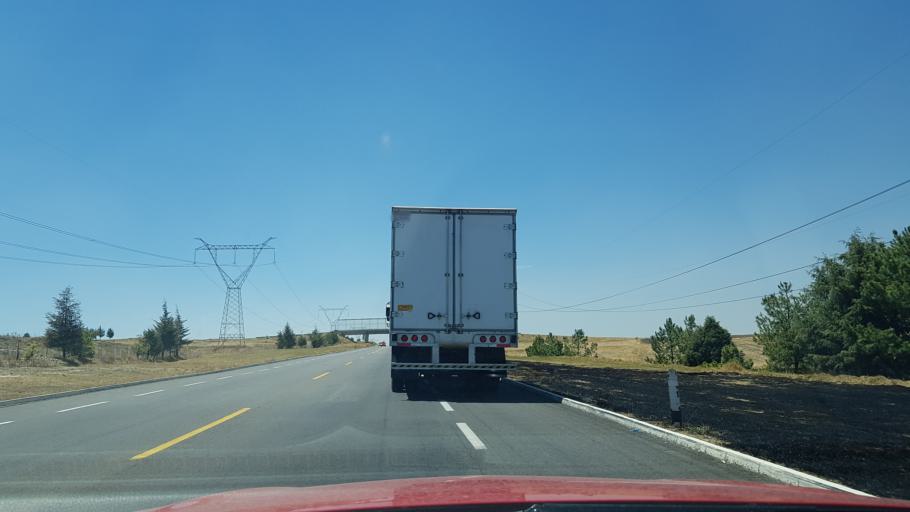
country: MX
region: Mexico
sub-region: Almoloya de Juarez
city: Conjunto Habitacional Ecologico SUTEYM
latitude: 19.3879
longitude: -99.7812
